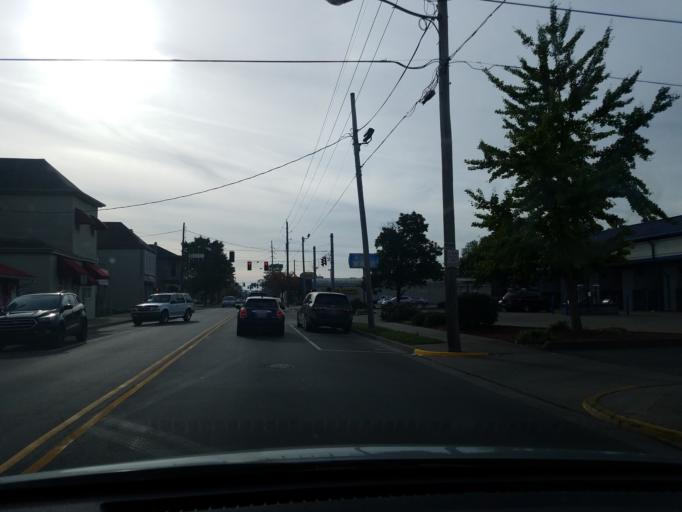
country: US
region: Indiana
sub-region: Floyd County
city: New Albany
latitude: 38.2942
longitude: -85.8085
